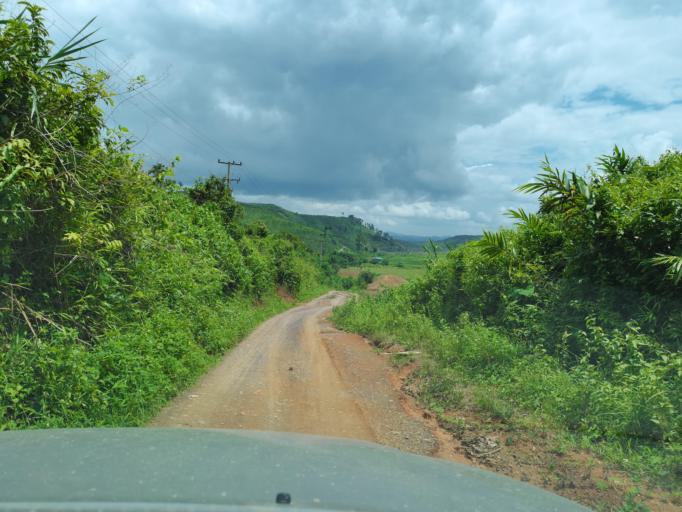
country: LA
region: Loungnamtha
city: Muang Long
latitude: 20.7280
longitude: 101.0141
